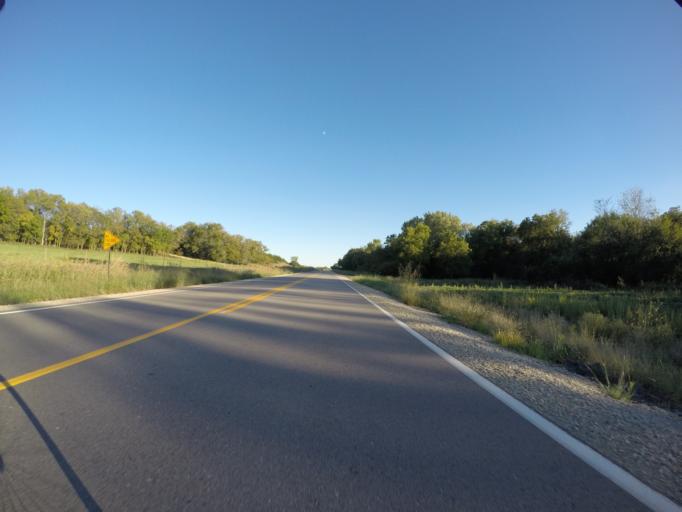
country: US
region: Kansas
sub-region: Riley County
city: Fort Riley North
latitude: 39.2556
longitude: -96.7736
